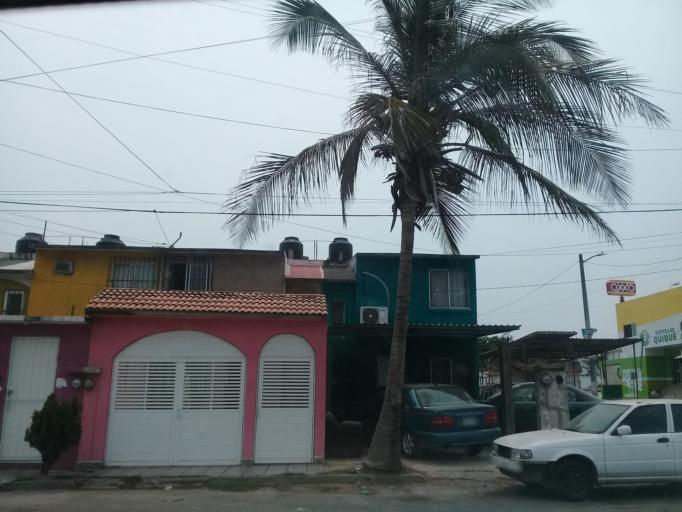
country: MX
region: Veracruz
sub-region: Veracruz
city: Rio Medio [Granja]
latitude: 19.2108
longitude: -96.2011
